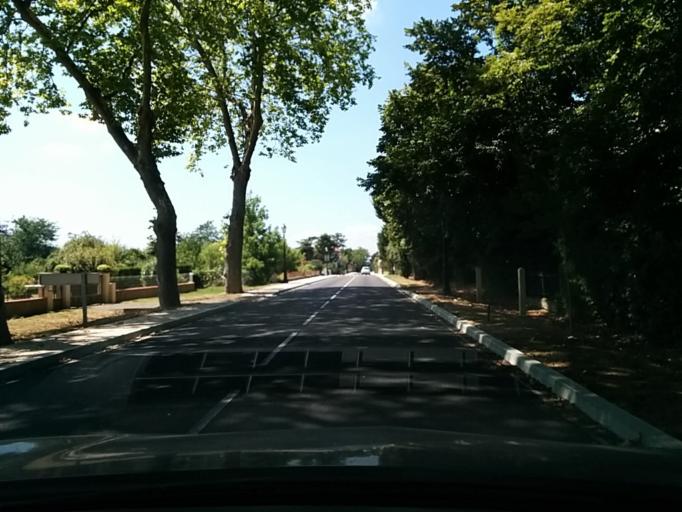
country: FR
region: Midi-Pyrenees
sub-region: Departement du Gers
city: Le Houga
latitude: 43.7681
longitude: -0.1214
